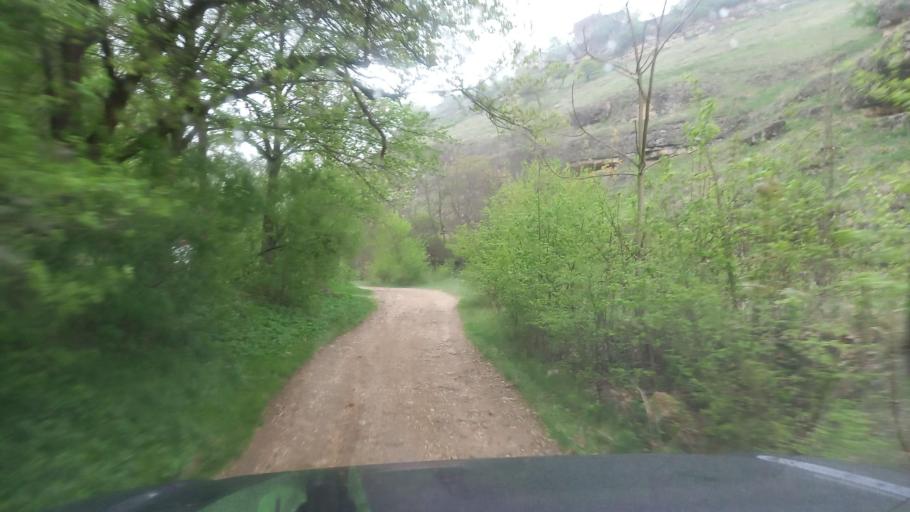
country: RU
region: Stavropol'skiy
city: Kislovodsk
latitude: 43.8884
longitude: 42.7053
